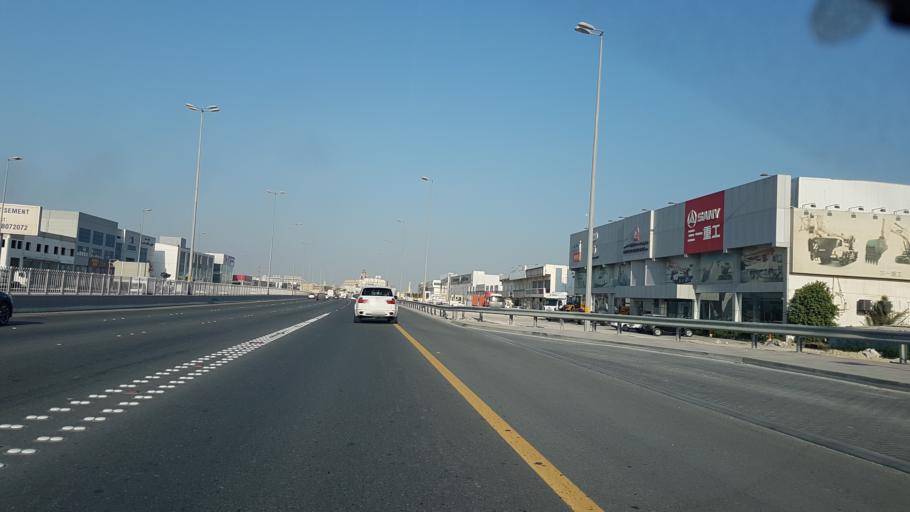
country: BH
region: Northern
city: Sitrah
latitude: 26.1333
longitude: 50.6052
